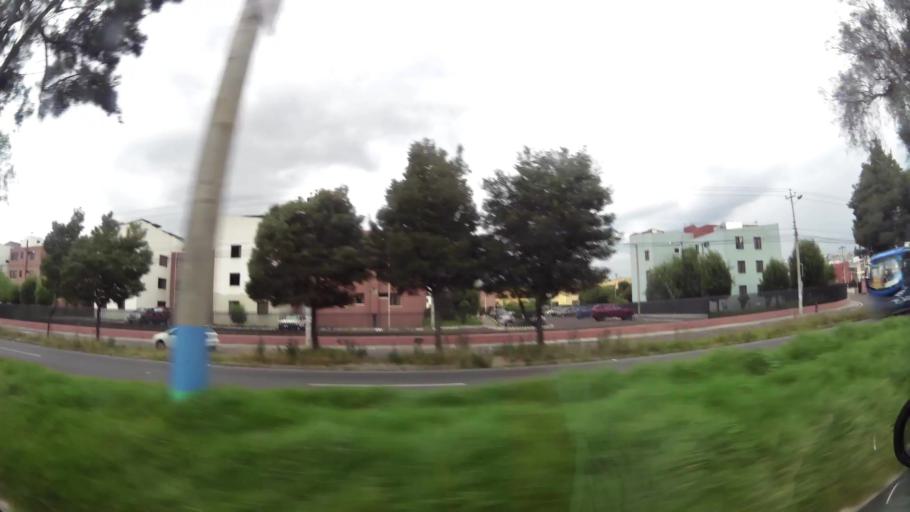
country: EC
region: Pichincha
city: Quito
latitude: -0.0691
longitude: -78.4693
